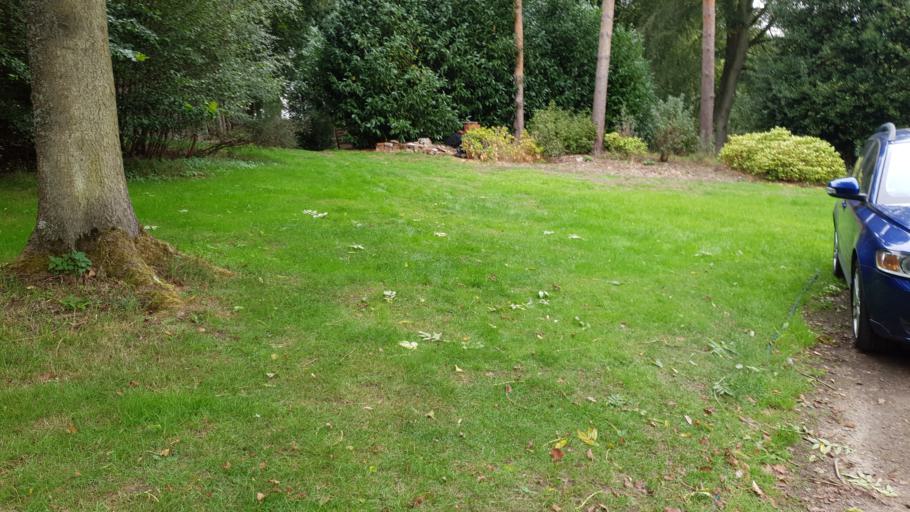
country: GB
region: England
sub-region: Suffolk
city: East Bergholt
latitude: 51.9408
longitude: 1.0173
